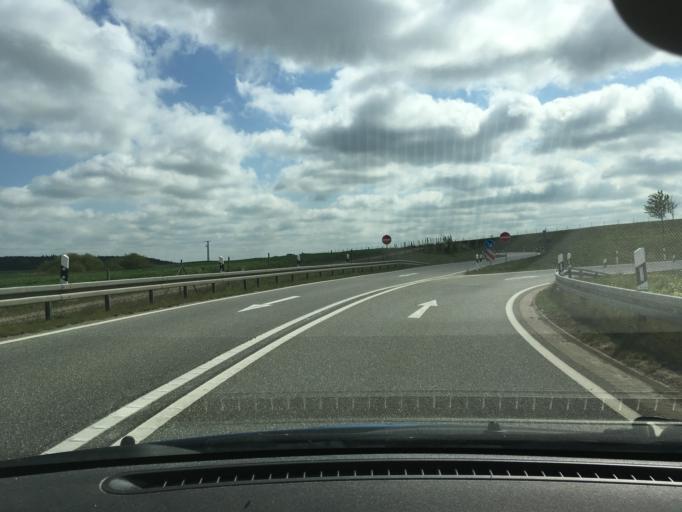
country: DE
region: Mecklenburg-Vorpommern
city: Zurow
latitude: 53.8058
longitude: 11.6092
